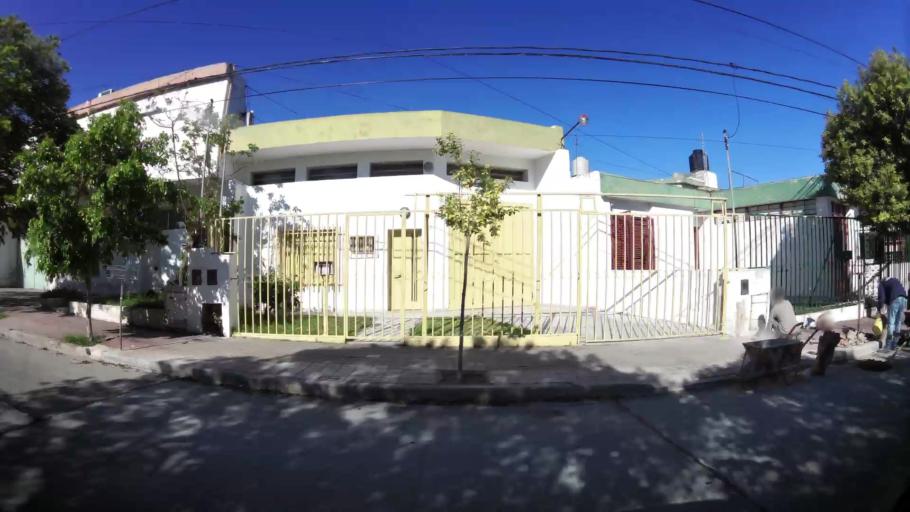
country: AR
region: Cordoba
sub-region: Departamento de Capital
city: Cordoba
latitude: -31.4257
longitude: -64.1386
